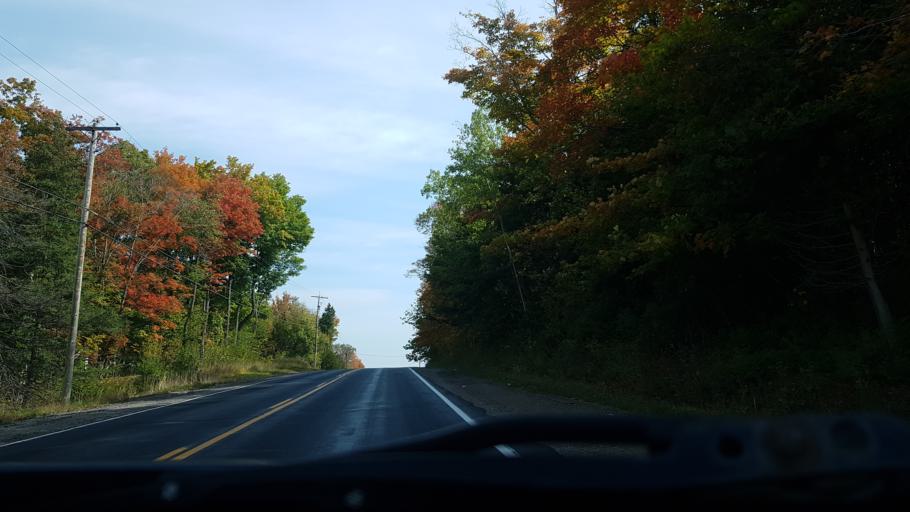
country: CA
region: Ontario
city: Orillia
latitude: 44.6394
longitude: -79.1705
